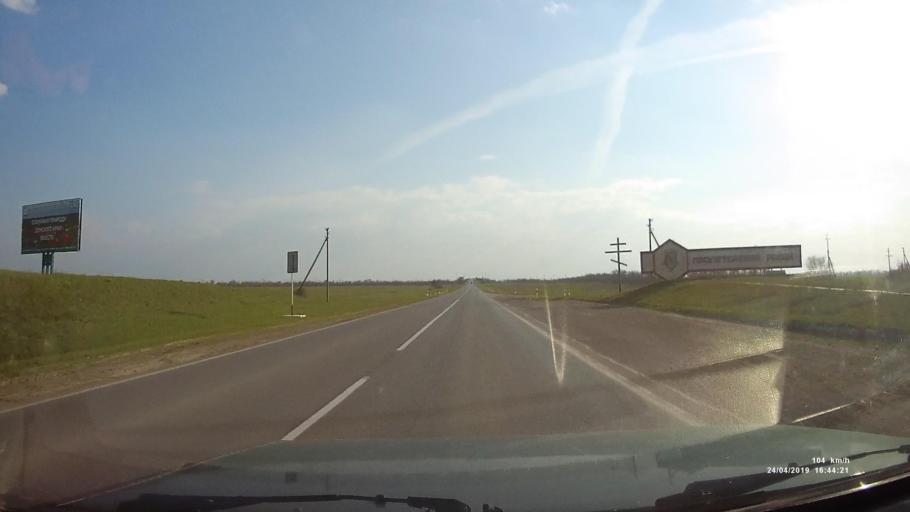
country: RU
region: Rostov
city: Gundorovskiy
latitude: 46.7829
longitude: 41.8283
